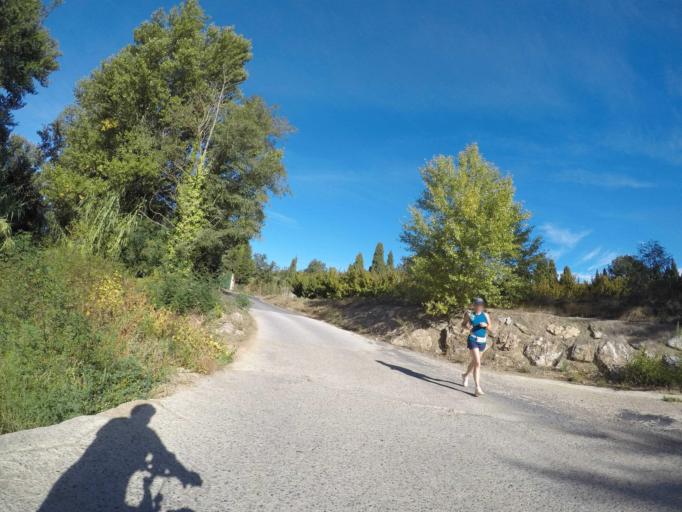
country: FR
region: Languedoc-Roussillon
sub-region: Departement des Pyrenees-Orientales
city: Trouillas
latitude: 42.5871
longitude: 2.8097
